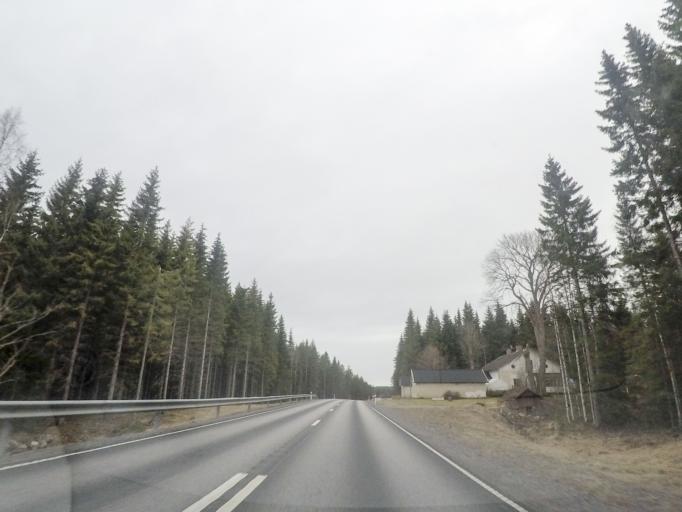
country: SE
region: OErebro
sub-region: Ljusnarsbergs Kommun
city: Kopparberg
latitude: 59.9671
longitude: 15.0200
